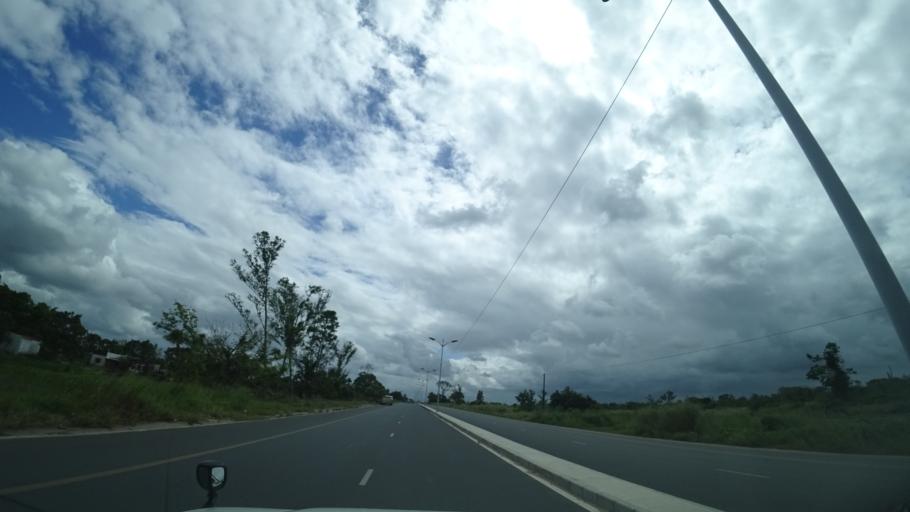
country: MZ
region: Sofala
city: Dondo
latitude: -19.5947
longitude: 34.7388
